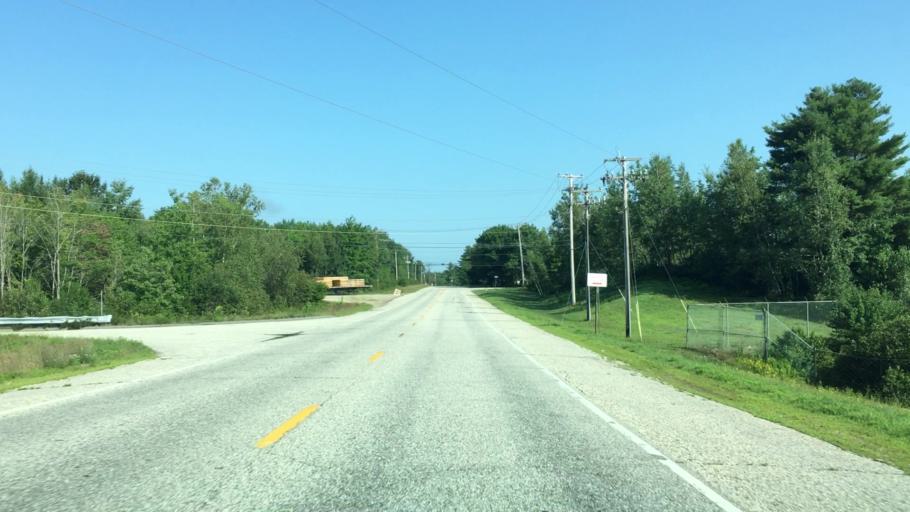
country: US
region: Maine
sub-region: Androscoggin County
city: Minot
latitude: 44.0416
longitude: -70.2913
